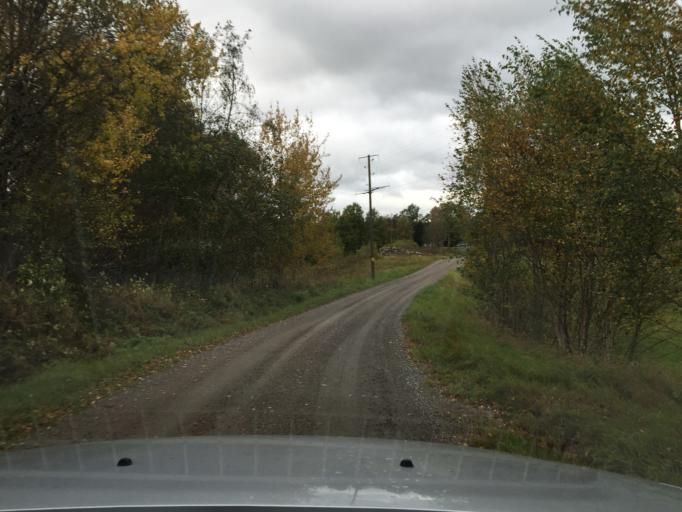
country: SE
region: Skane
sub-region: Hassleholms Kommun
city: Tormestorp
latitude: 56.0698
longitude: 13.7448
